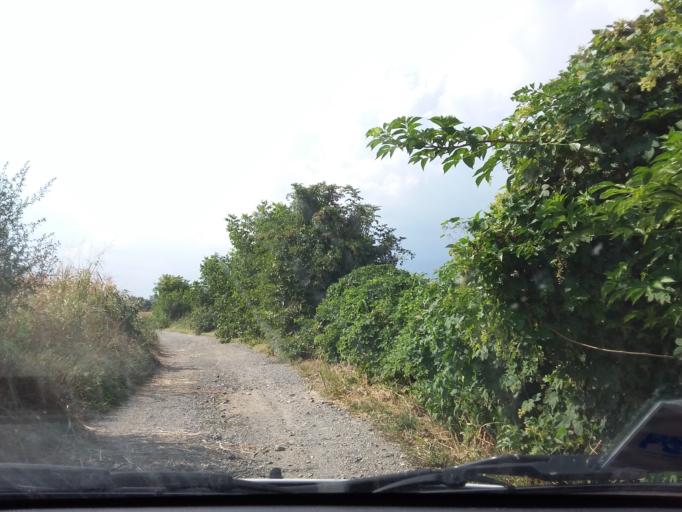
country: IT
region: Piedmont
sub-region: Provincia di Torino
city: Pianezza
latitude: 45.0868
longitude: 7.5415
